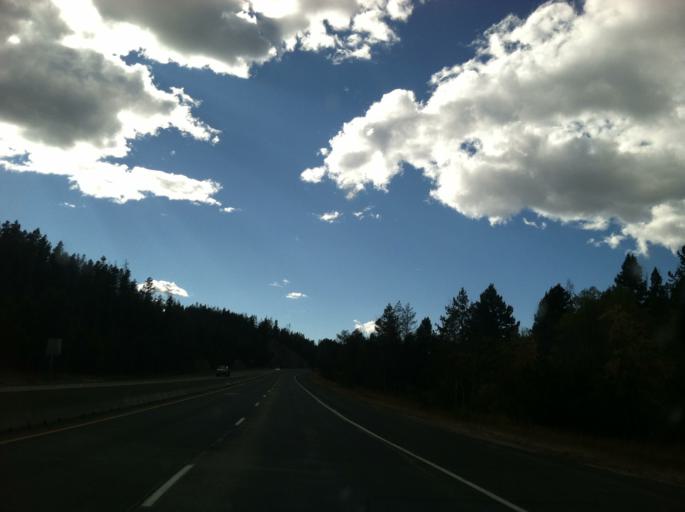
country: US
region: Montana
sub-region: Silver Bow County
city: Butte
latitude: 45.9156
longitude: -112.3829
